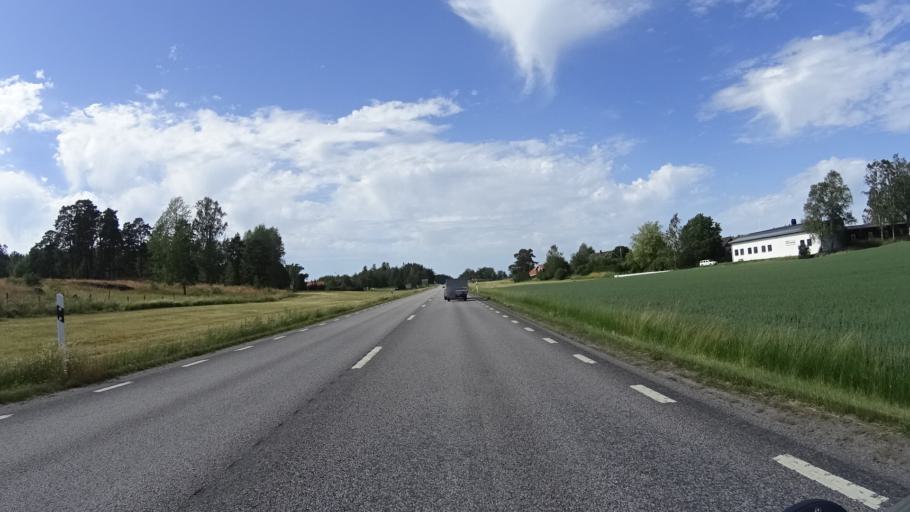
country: SE
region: OEstergoetland
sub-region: Linkopings Kommun
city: Linghem
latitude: 58.3500
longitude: 15.8379
